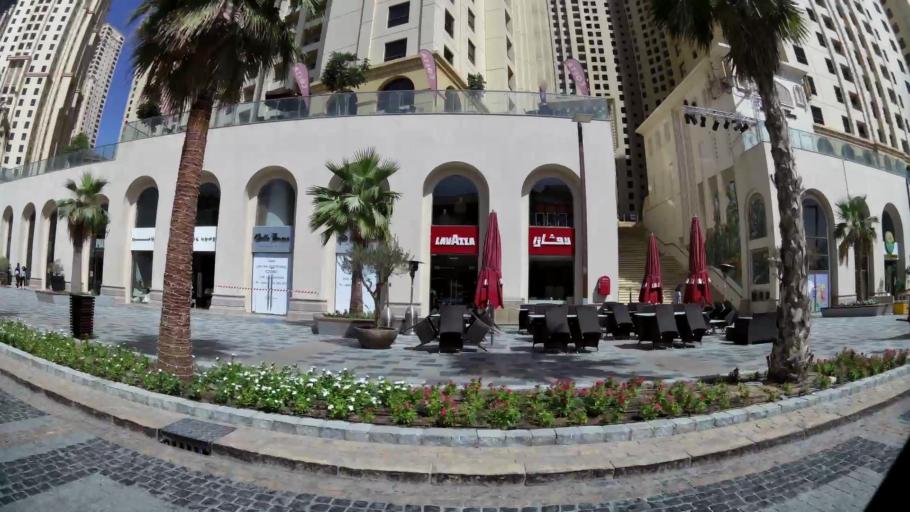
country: AE
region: Dubai
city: Dubai
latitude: 25.0816
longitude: 55.1375
